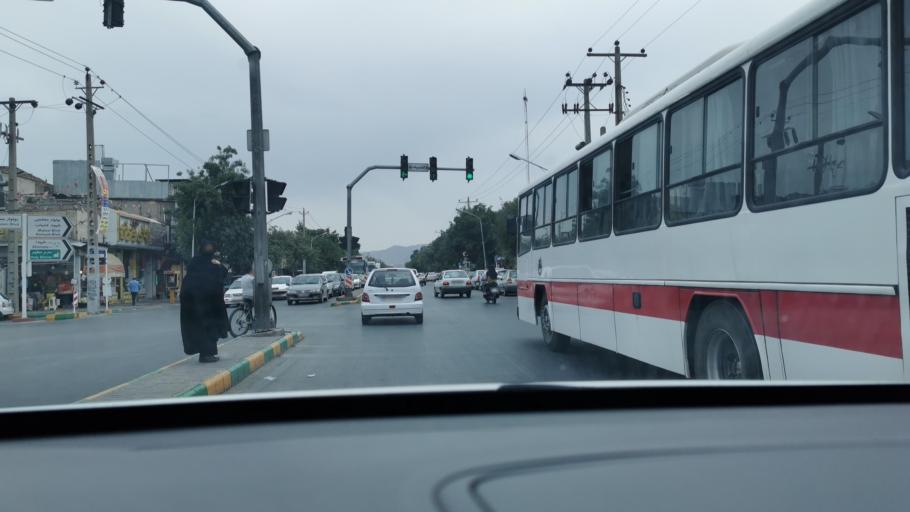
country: IR
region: Razavi Khorasan
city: Mashhad
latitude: 36.3179
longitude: 59.6182
